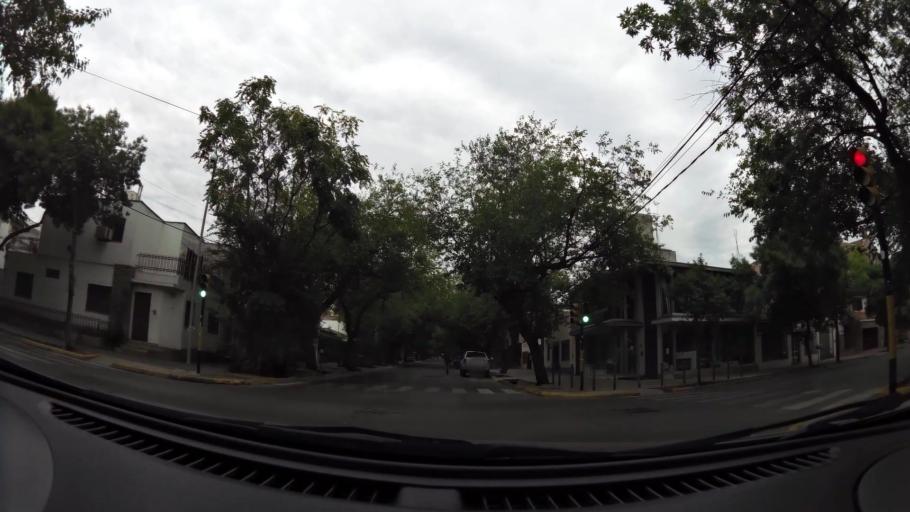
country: AR
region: Mendoza
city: Mendoza
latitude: -32.9006
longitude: -68.8479
